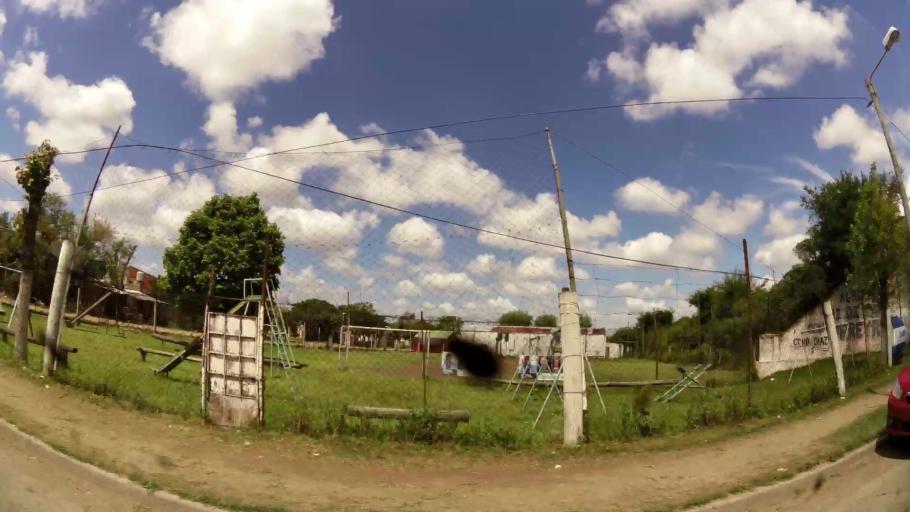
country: AR
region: Buenos Aires
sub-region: Partido de Quilmes
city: Quilmes
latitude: -34.8221
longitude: -58.2426
